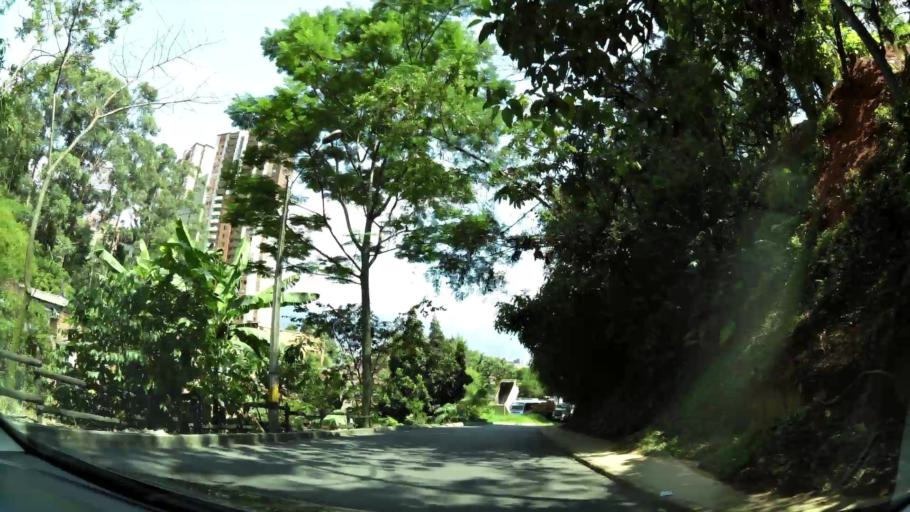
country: CO
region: Antioquia
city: Itagui
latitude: 6.2162
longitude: -75.6031
